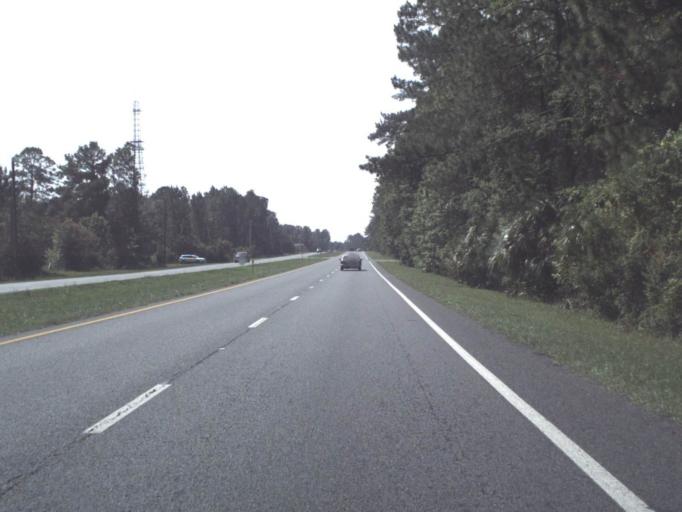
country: US
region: Florida
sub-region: Nassau County
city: Hilliard
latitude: 30.6529
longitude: -81.8759
